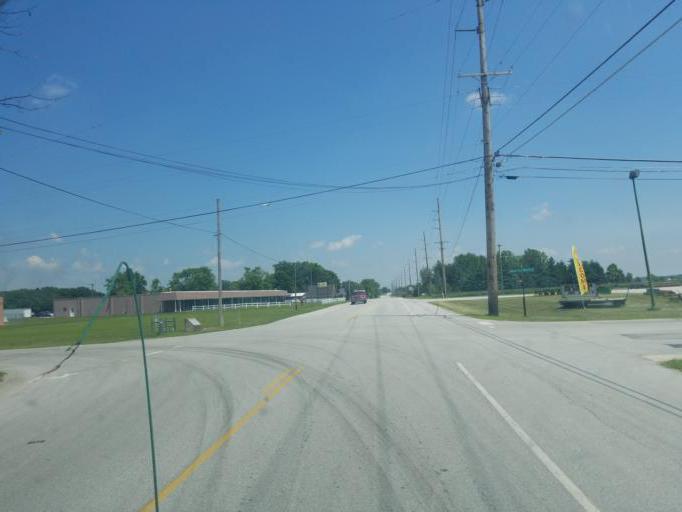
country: US
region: Ohio
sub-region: Auglaize County
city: Saint Marys
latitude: 40.5560
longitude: -84.2985
